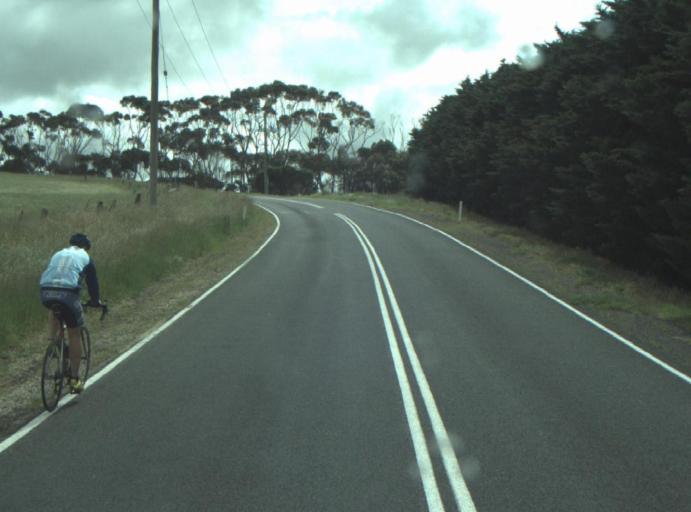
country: AU
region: Victoria
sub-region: Greater Geelong
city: Wandana Heights
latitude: -38.1930
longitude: 144.2668
